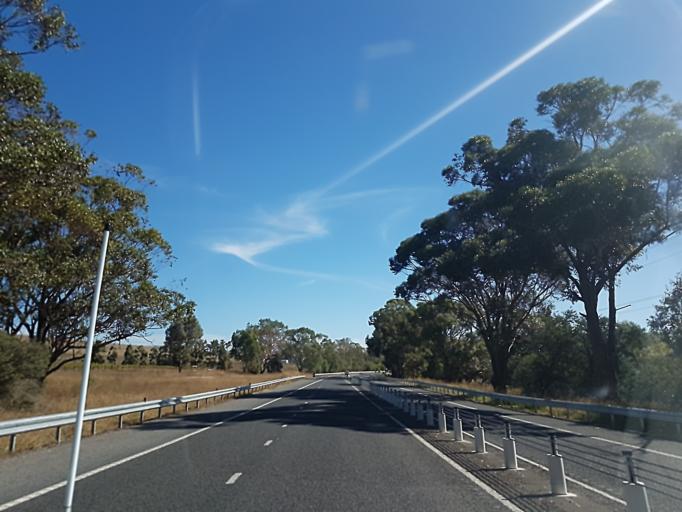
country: AU
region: Victoria
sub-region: Murrindindi
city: Alexandra
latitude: -37.2078
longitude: 145.4568
